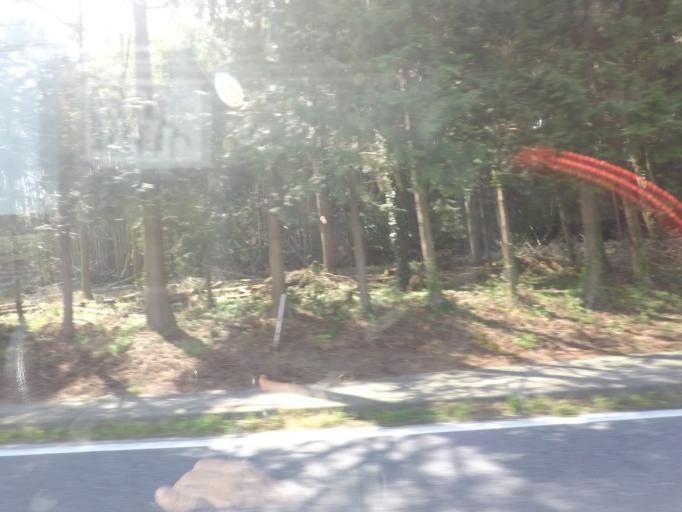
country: JP
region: Chiba
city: Narita
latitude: 35.8121
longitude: 140.3107
